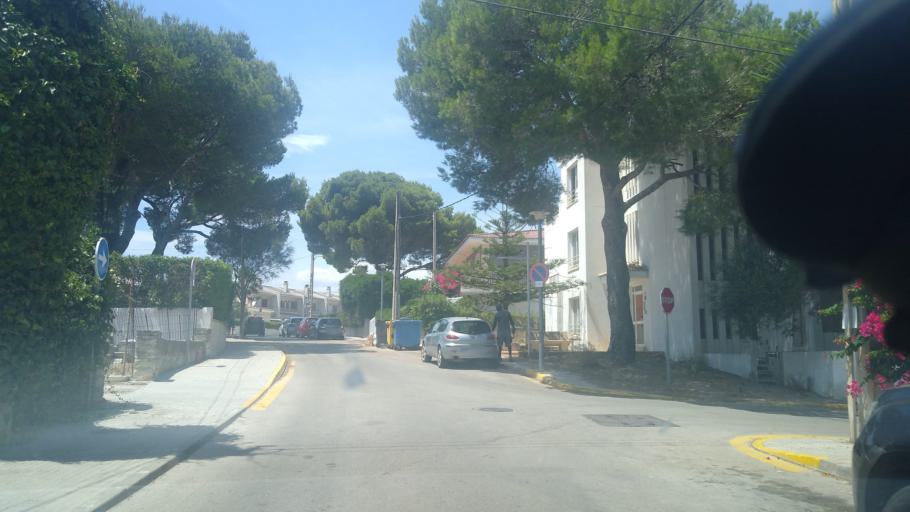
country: ES
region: Balearic Islands
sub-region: Illes Balears
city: Santa Margalida
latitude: 39.7581
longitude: 3.1664
